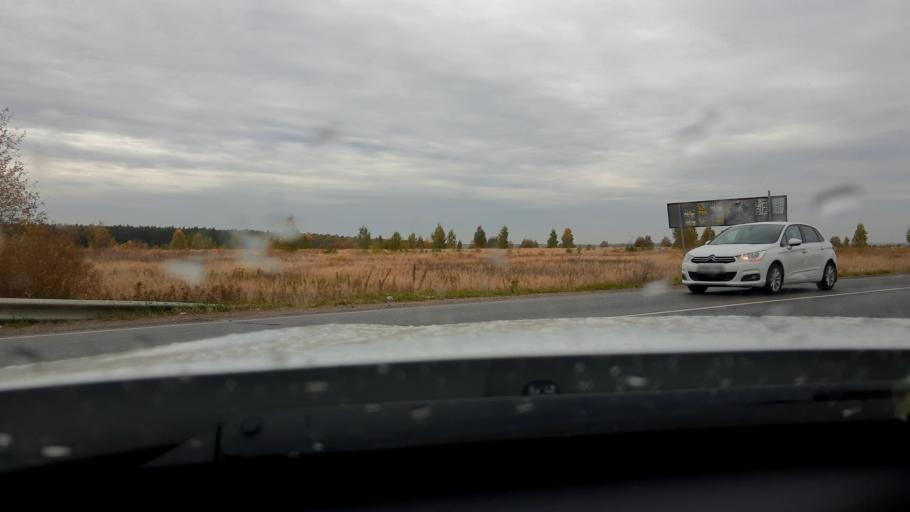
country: RU
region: Moskovskaya
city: Domodedovo
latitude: 55.4179
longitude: 37.6967
